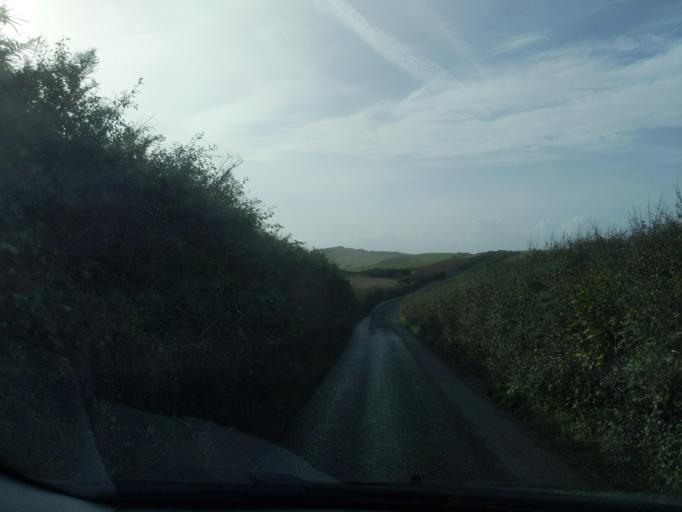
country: GB
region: England
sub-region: Cornwall
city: Pillaton
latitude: 50.3640
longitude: -4.3213
